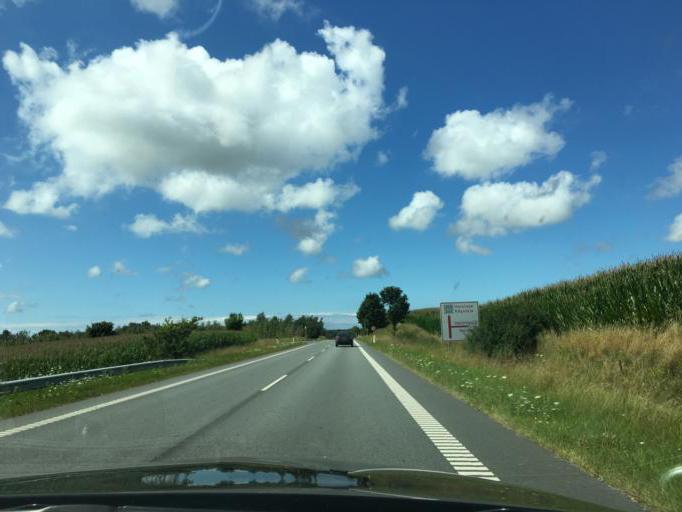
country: DK
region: Capital Region
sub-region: Gribskov Kommune
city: Helsinge
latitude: 56.0280
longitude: 12.2304
